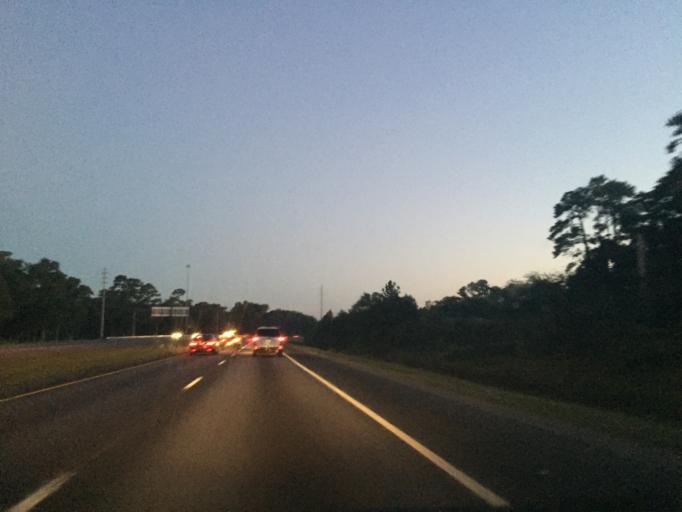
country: US
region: Georgia
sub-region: Chatham County
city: Isle of Hope
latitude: 32.0082
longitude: -81.0800
